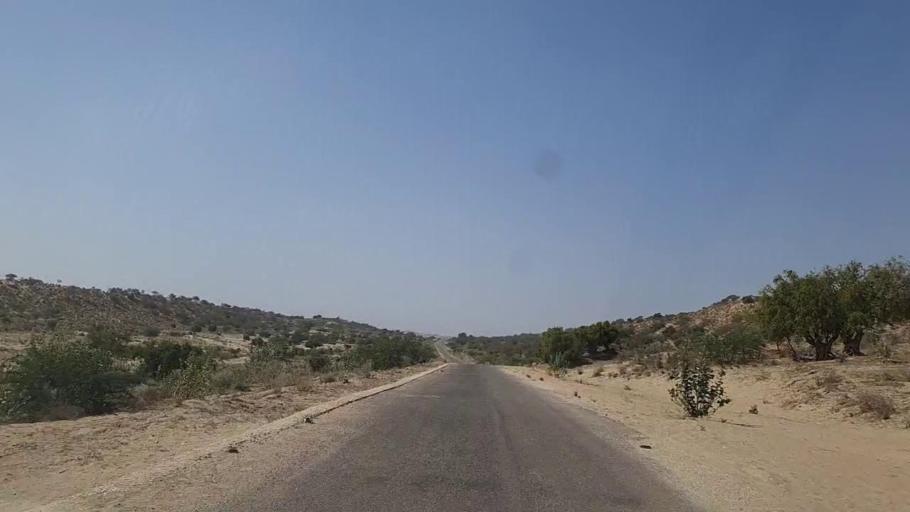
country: PK
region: Sindh
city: Diplo
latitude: 24.5740
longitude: 69.4789
